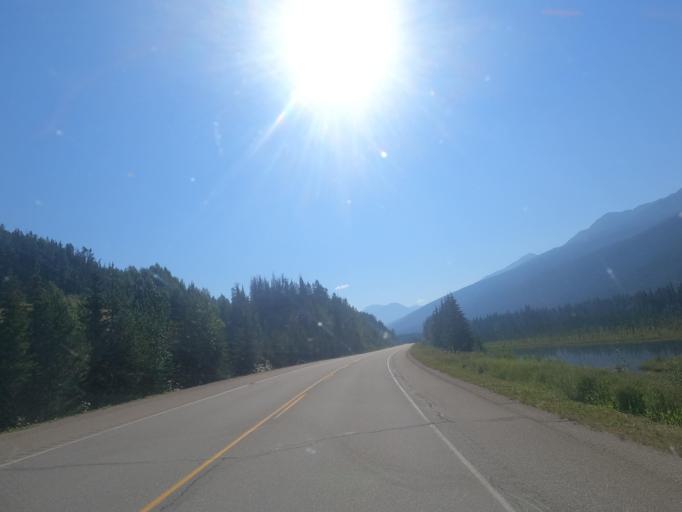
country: CA
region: Alberta
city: Jasper Park Lodge
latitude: 52.8917
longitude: -118.7306
